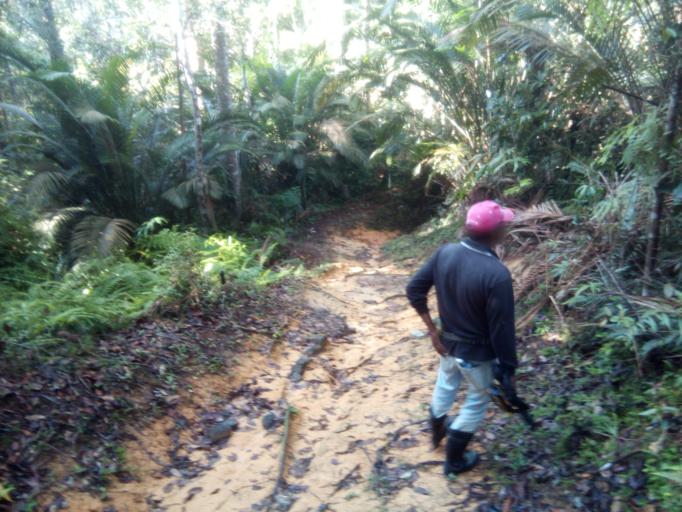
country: MY
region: Penang
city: Tanjung Tokong
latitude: 5.4174
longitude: 100.2582
